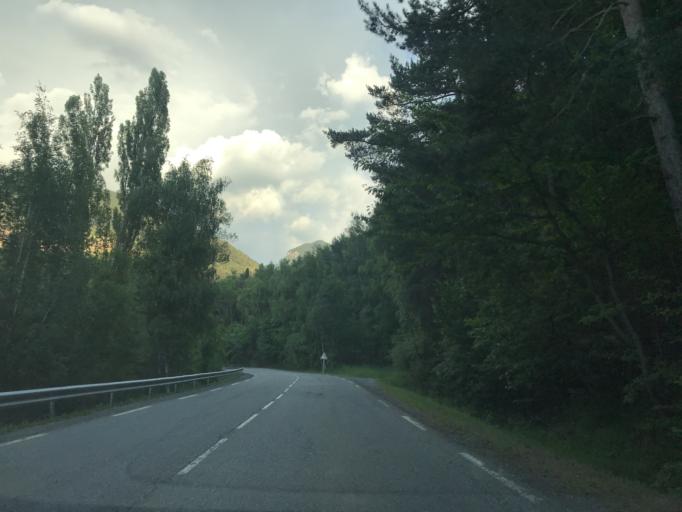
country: FR
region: Provence-Alpes-Cote d'Azur
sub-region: Departement des Hautes-Alpes
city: Guillestre
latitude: 44.6545
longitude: 6.6527
